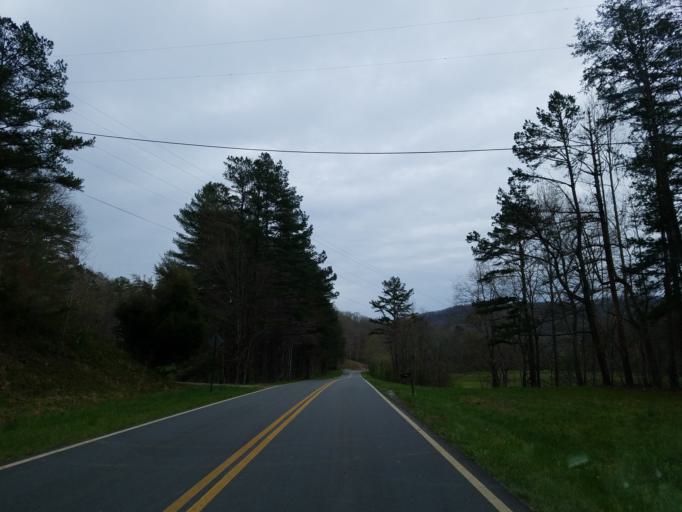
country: US
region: Georgia
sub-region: Fannin County
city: Blue Ridge
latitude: 34.8433
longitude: -84.2997
